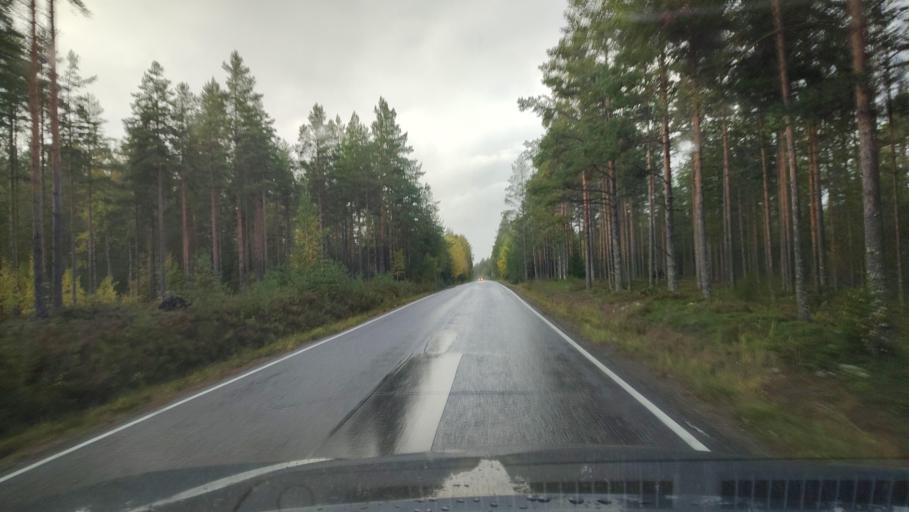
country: FI
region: Southern Ostrobothnia
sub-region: Suupohja
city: Karijoki
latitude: 62.3214
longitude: 21.6766
